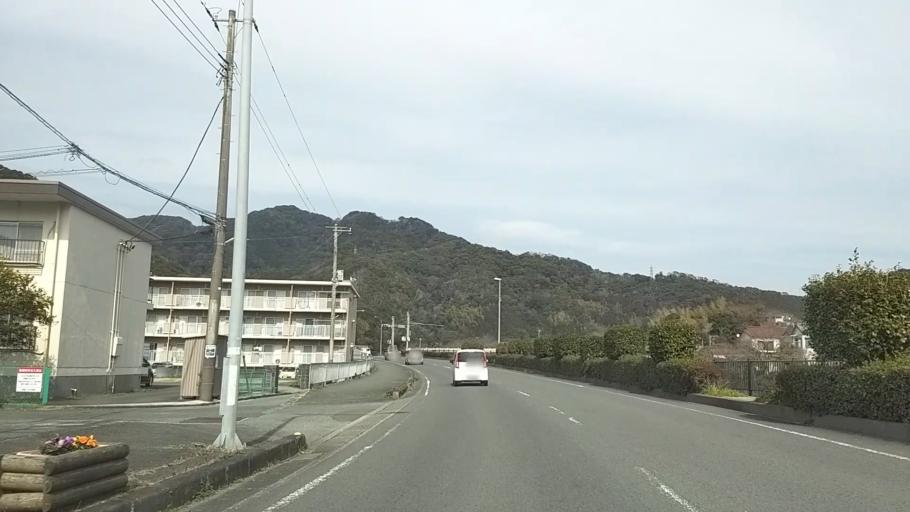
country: JP
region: Shizuoka
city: Shimoda
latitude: 34.7016
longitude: 138.9406
